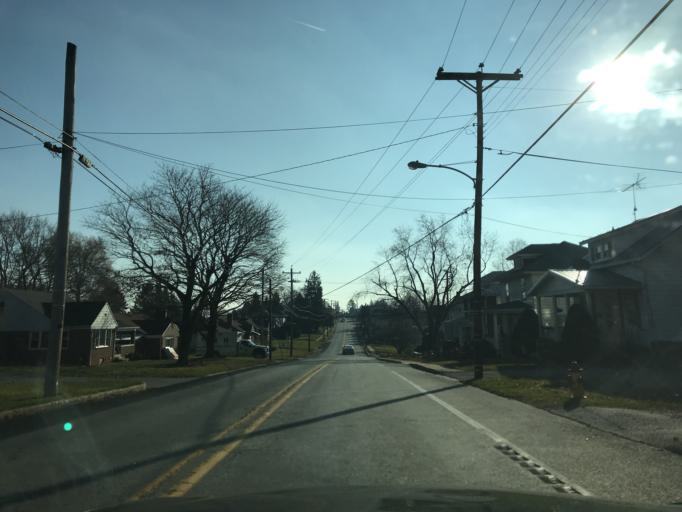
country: US
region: Pennsylvania
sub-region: York County
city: Shrewsbury
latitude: 39.7750
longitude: -76.6802
